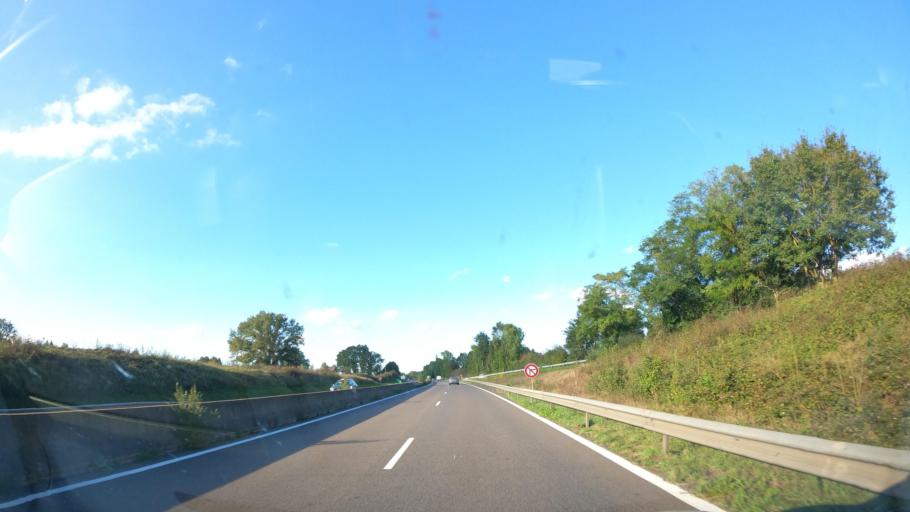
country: FR
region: Bourgogne
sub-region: Departement de Saone-et-Loire
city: Saint-Vallier
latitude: 46.6440
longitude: 4.3297
